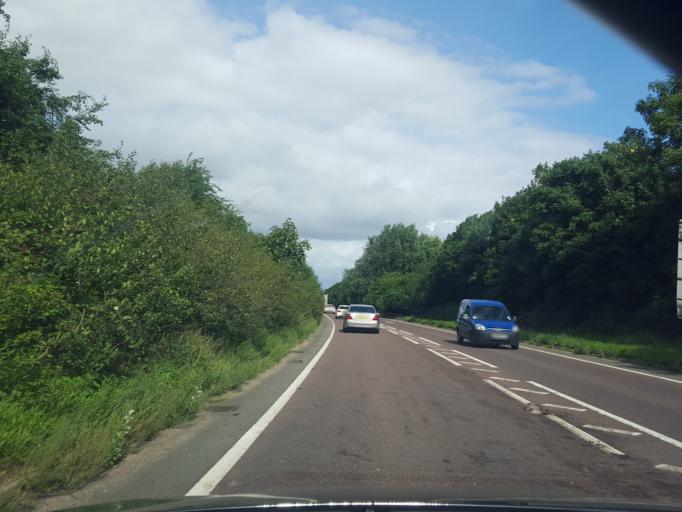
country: GB
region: England
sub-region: Essex
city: Dovercourt
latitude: 51.9348
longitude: 1.2492
